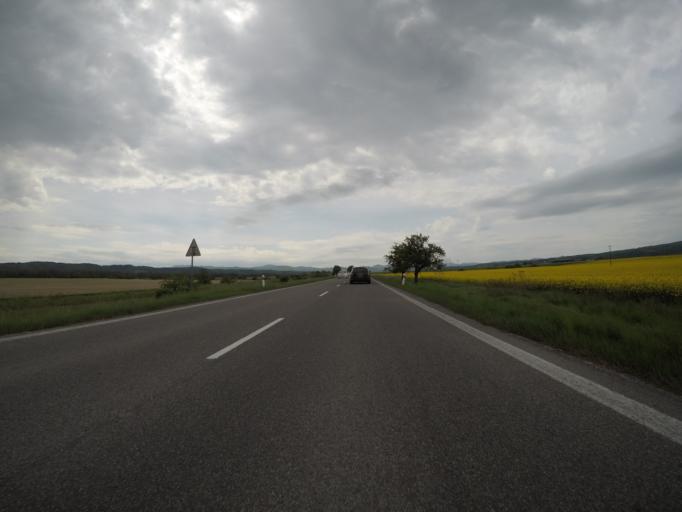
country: SK
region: Banskobystricky
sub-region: Okres Banska Bystrica
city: Zvolen
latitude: 48.6542
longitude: 19.1436
